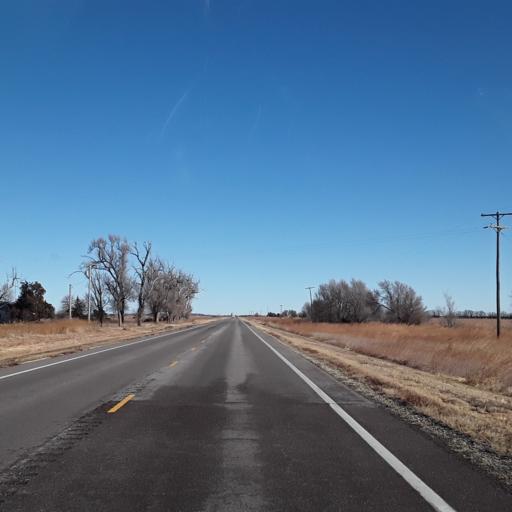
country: US
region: Kansas
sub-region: Pawnee County
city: Larned
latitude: 38.1239
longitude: -99.1736
